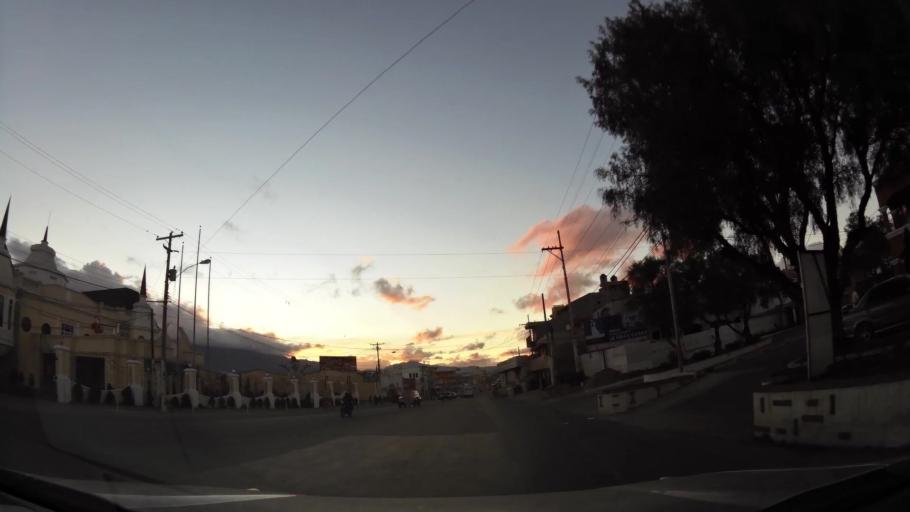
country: GT
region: Quetzaltenango
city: Olintepeque
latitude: 14.8592
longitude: -91.5178
